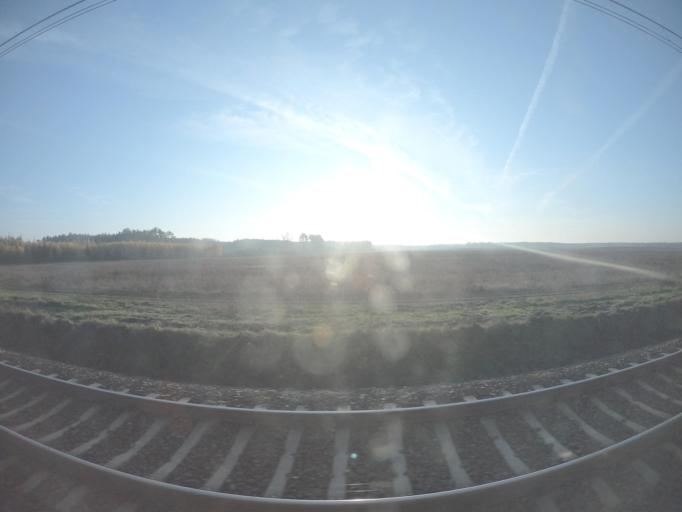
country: PL
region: Lubusz
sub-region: Powiat slubicki
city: Rzepin
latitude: 52.2904
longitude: 14.8891
